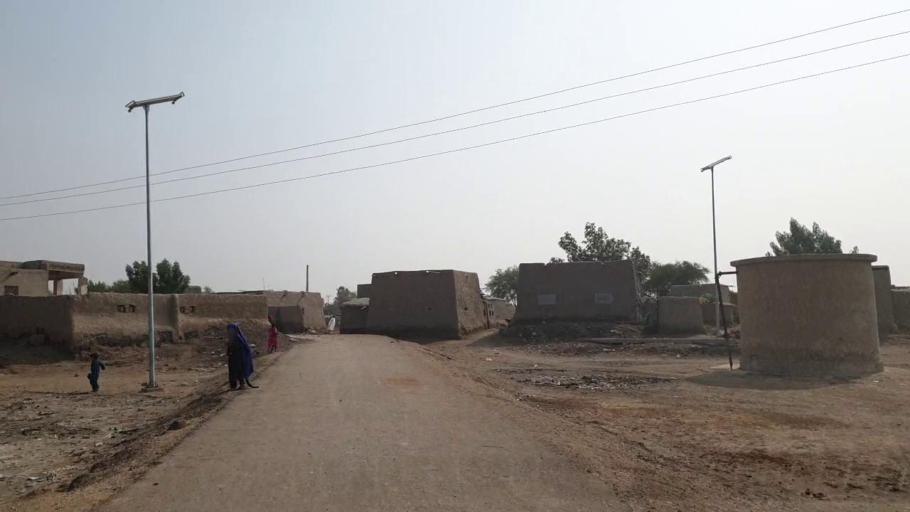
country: PK
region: Sindh
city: Bhan
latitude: 26.4564
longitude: 67.6944
